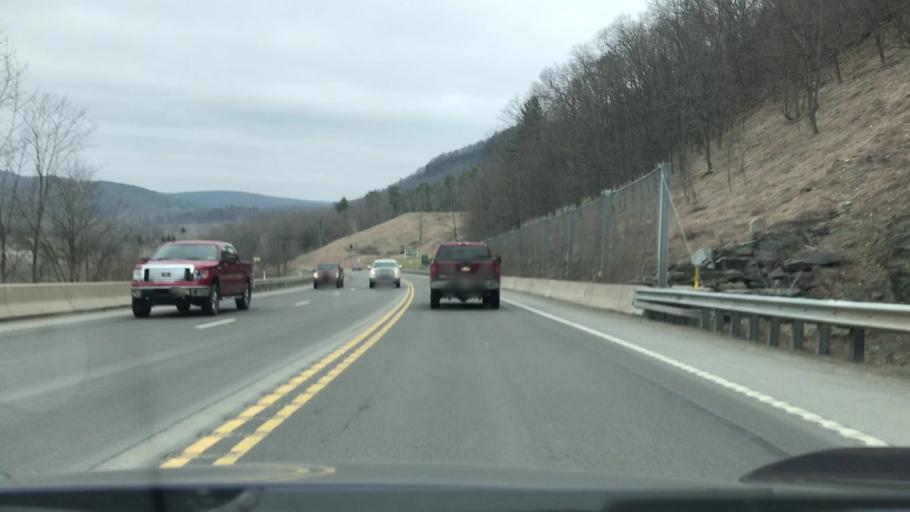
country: US
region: Pennsylvania
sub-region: Bradford County
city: Towanda
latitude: 41.7693
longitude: -76.3692
